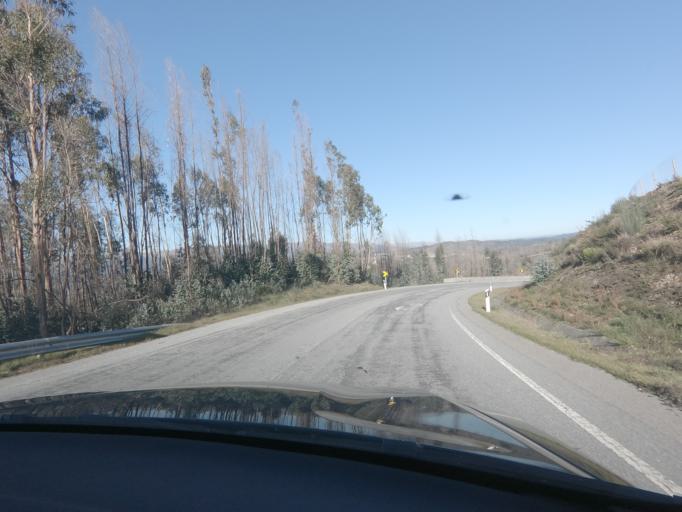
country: PT
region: Viseu
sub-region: Vouzela
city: Vouzela
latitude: 40.7242
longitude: -8.1318
